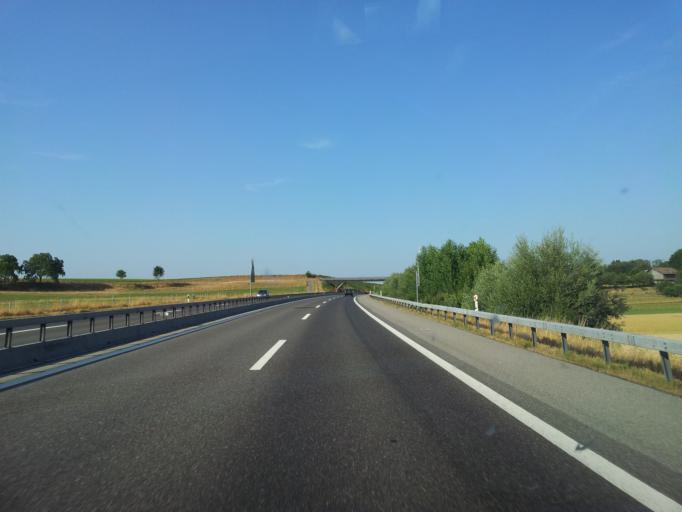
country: CH
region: Fribourg
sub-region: Sense District
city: Ueberstorf
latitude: 46.8827
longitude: 7.2868
